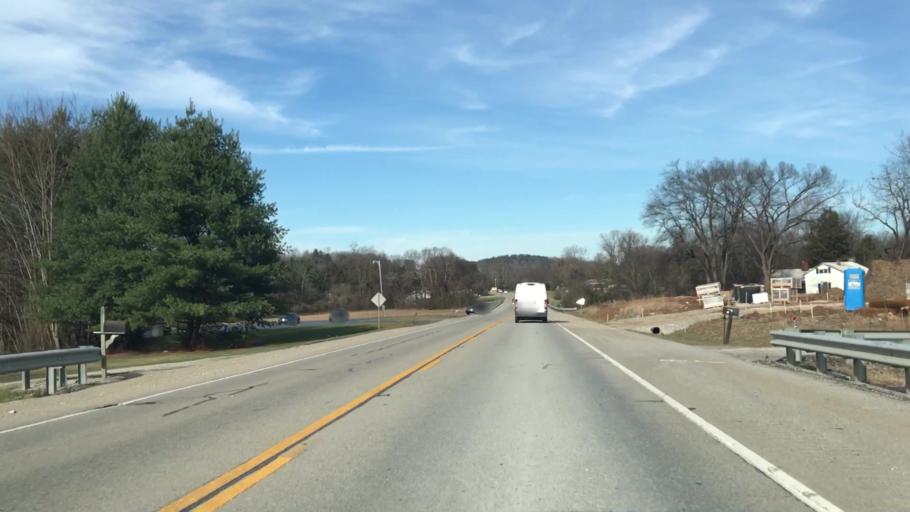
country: US
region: Kentucky
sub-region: Pulaski County
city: Somerset
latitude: 36.9572
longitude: -84.5822
